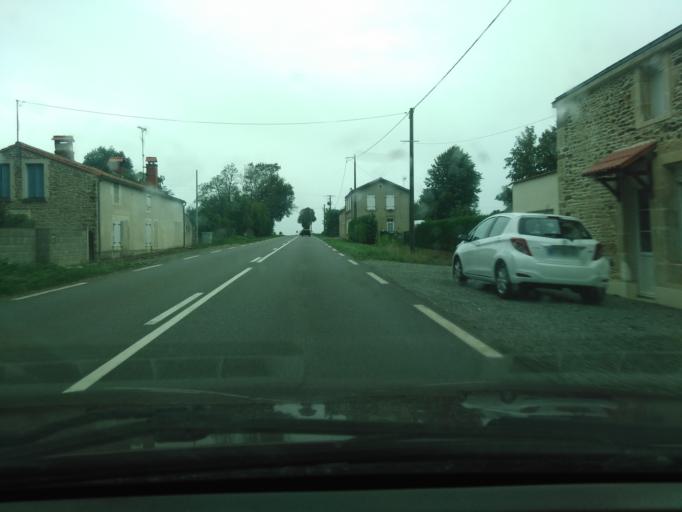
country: FR
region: Pays de la Loire
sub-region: Departement de la Vendee
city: Sainte-Hermine
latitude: 46.5707
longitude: -1.0895
